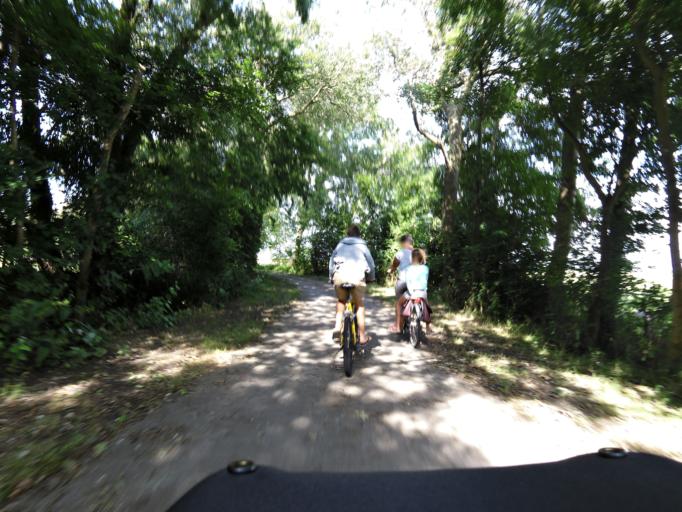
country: NL
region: South Holland
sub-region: Gemeente Goeree-Overflakkee
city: Ouddorp
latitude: 51.7969
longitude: 3.8698
